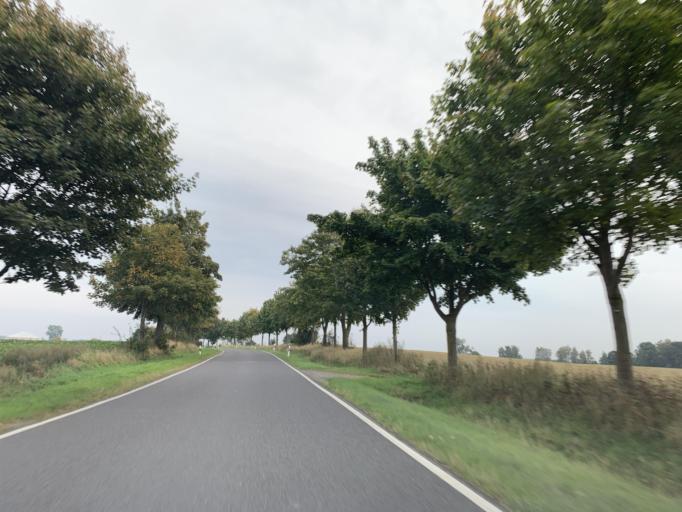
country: DE
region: Mecklenburg-Vorpommern
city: Woldegk
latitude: 53.3282
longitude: 13.5467
